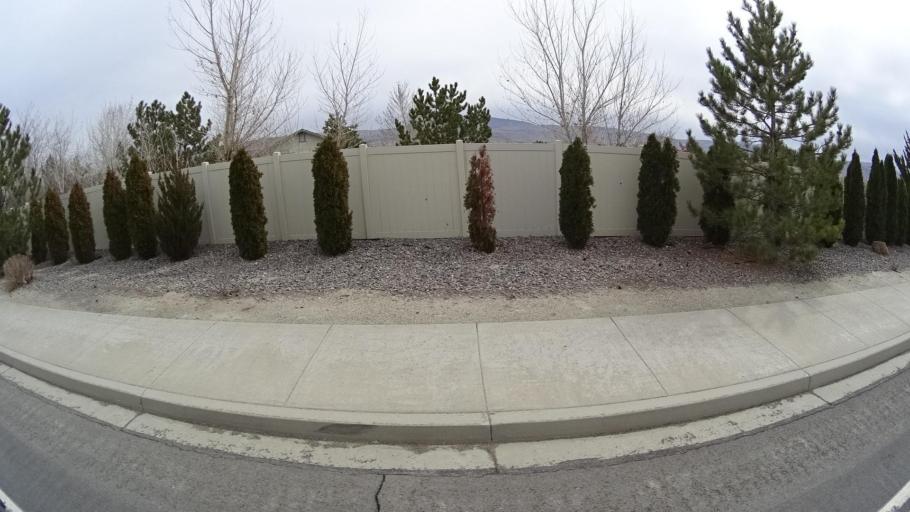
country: US
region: Nevada
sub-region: Washoe County
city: Spanish Springs
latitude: 39.6545
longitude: -119.7341
